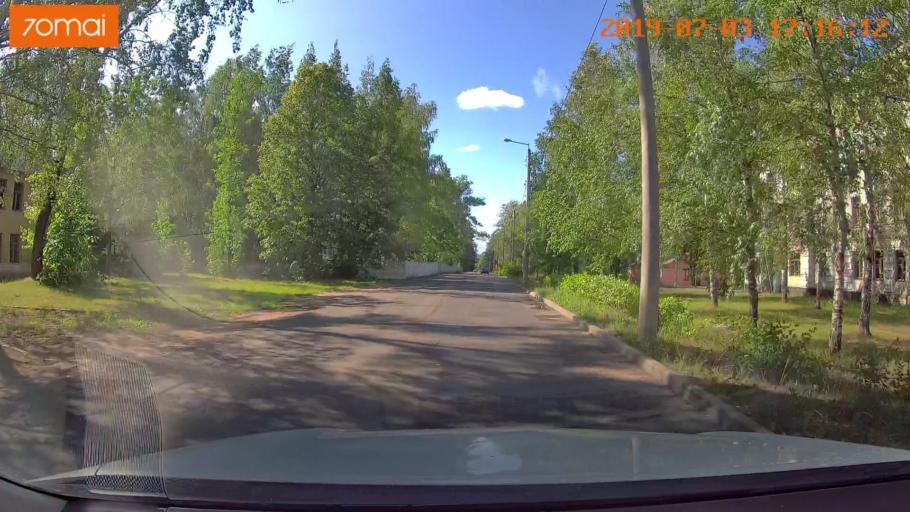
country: BY
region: Minsk
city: Vyaliki Trastsyanets
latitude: 53.9052
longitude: 27.6783
